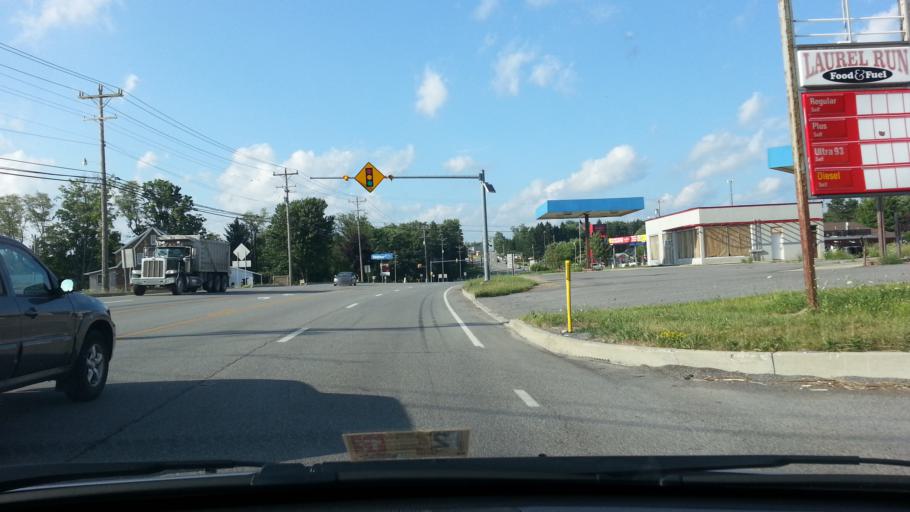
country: US
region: Pennsylvania
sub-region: Elk County
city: Saint Marys
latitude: 41.3890
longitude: -78.5590
